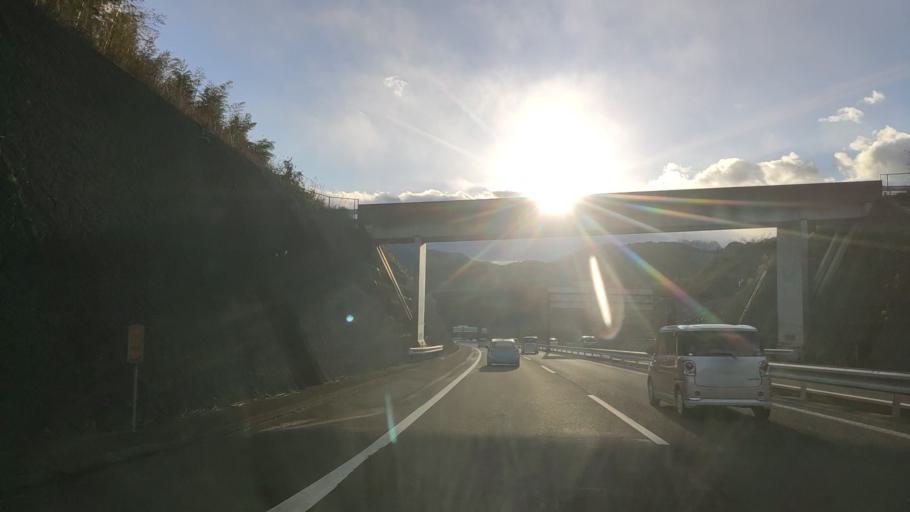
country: JP
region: Ehime
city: Saijo
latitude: 33.8808
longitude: 133.0856
